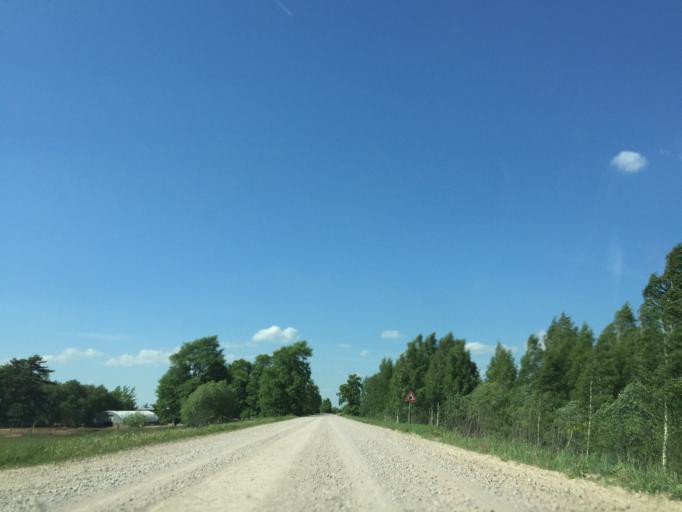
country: LV
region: Rundales
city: Pilsrundale
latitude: 56.5453
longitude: 23.9902
